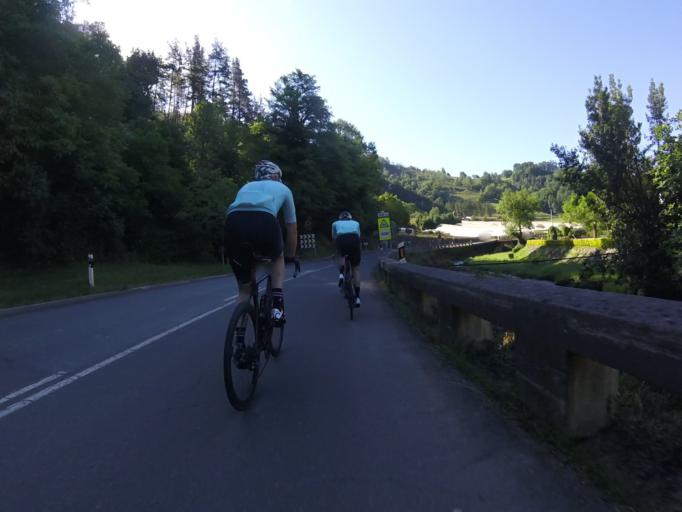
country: ES
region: Basque Country
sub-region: Provincia de Guipuzcoa
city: Beizama
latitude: 43.1468
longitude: -2.2326
